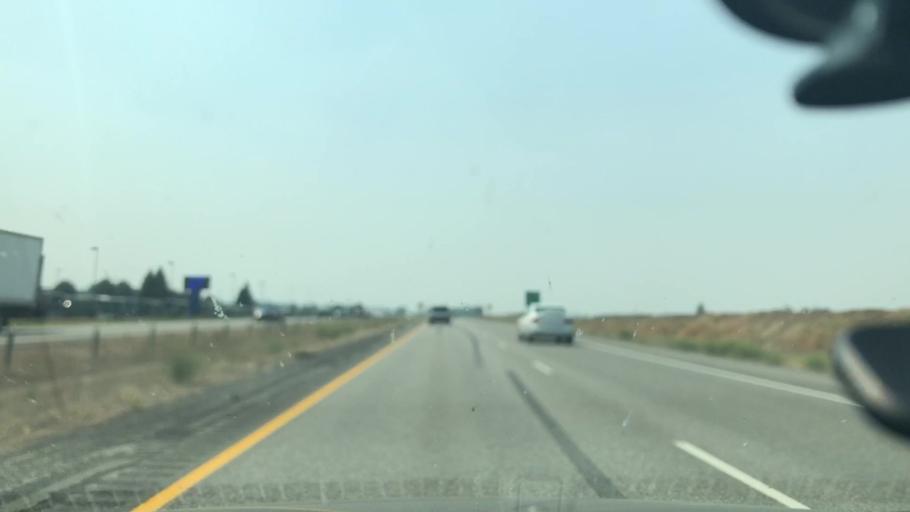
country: US
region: Washington
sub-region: Spokane County
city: Liberty Lake
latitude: 47.6797
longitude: -117.0921
